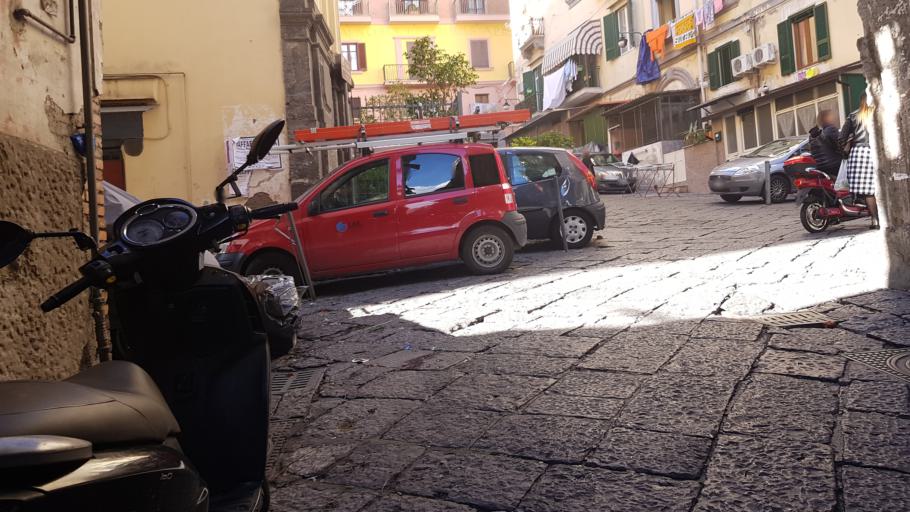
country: IT
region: Campania
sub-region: Provincia di Napoli
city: Napoli
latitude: 40.8396
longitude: 14.2449
